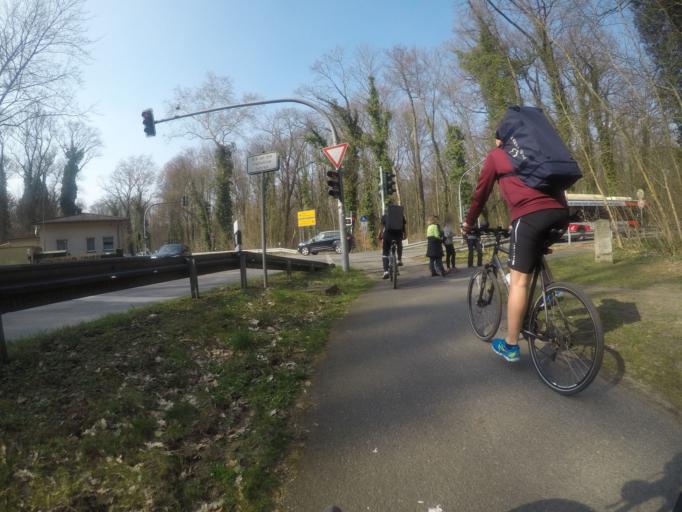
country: DE
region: Brandenburg
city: Konigs Wusterhausen
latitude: 52.2911
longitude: 13.6478
